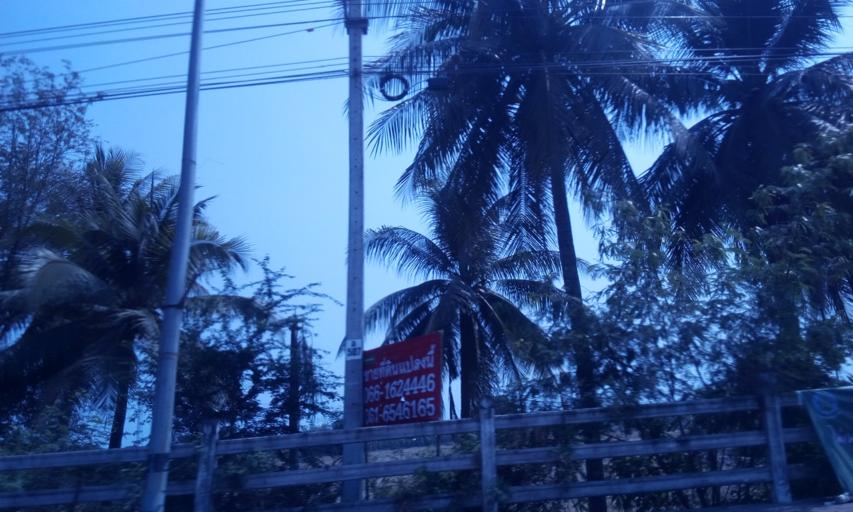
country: TH
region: Nonthaburi
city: Bang Yai
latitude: 13.9100
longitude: 100.3403
